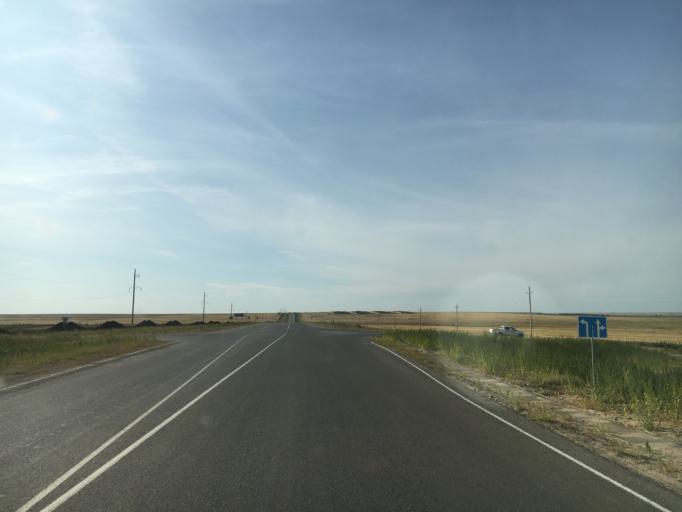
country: KZ
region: Batys Qazaqstan
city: Kamenka
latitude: 51.1196
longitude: 50.1909
